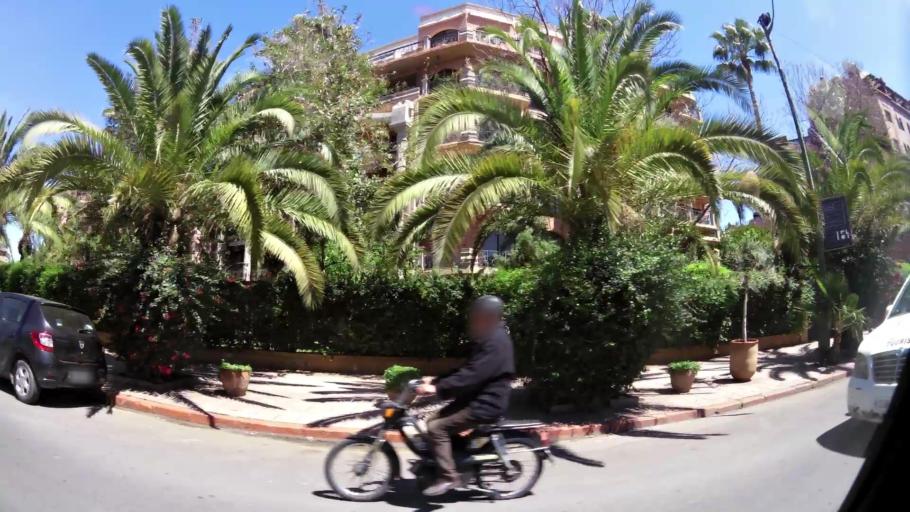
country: MA
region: Marrakech-Tensift-Al Haouz
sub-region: Marrakech
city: Marrakesh
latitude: 31.6222
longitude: -8.0019
